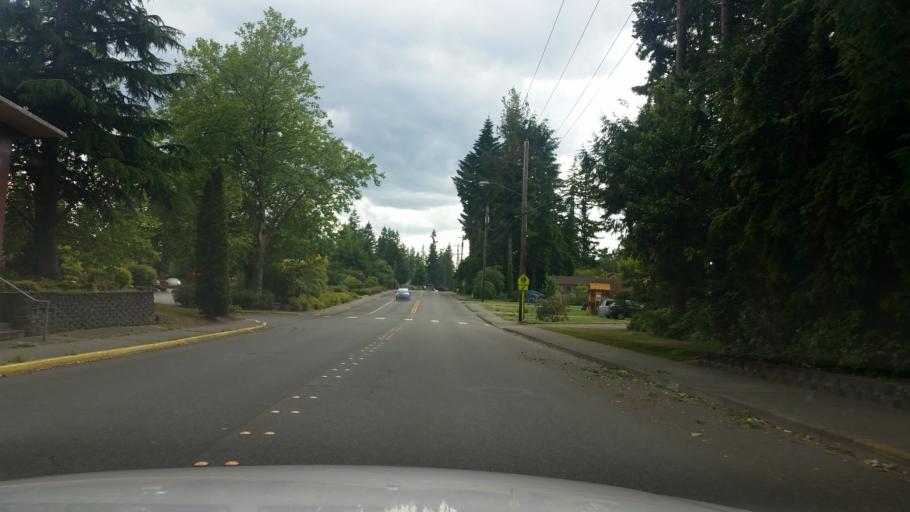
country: US
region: Washington
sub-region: Snohomish County
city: Mountlake Terrace
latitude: 47.7981
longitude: -122.3112
